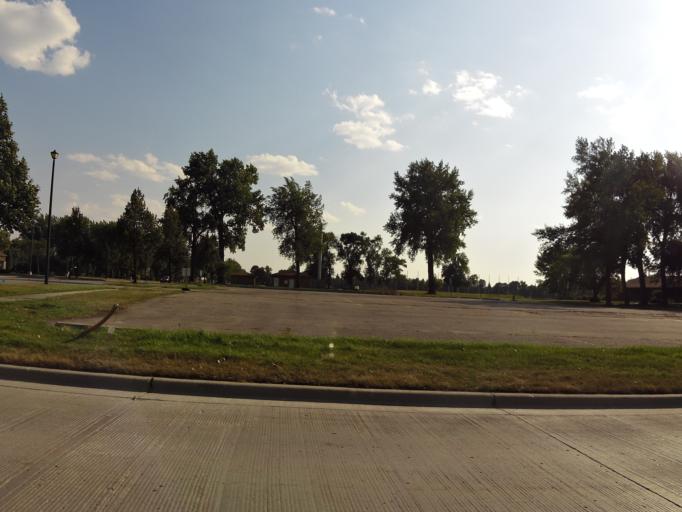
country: US
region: North Dakota
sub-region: Grand Forks County
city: Grand Forks
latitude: 47.9178
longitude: -97.0776
